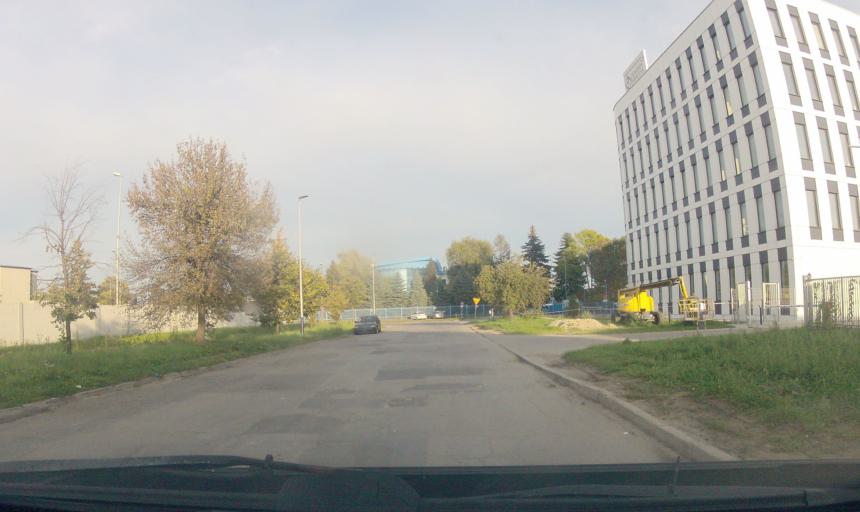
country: PL
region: Lesser Poland Voivodeship
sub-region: Powiat wielicki
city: Czarnochowice
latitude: 50.0363
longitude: 20.0168
